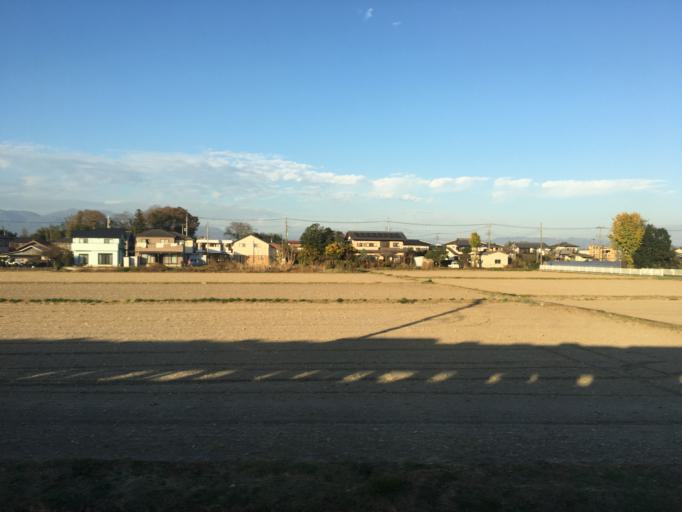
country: JP
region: Gunma
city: Isesaki
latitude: 36.3467
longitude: 139.1574
